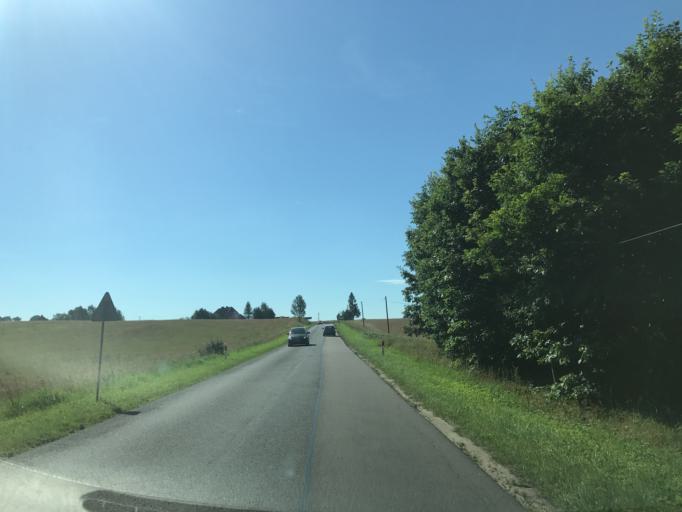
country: PL
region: Pomeranian Voivodeship
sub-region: Powiat bytowski
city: Czarna Dabrowka
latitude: 54.3693
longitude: 17.5024
